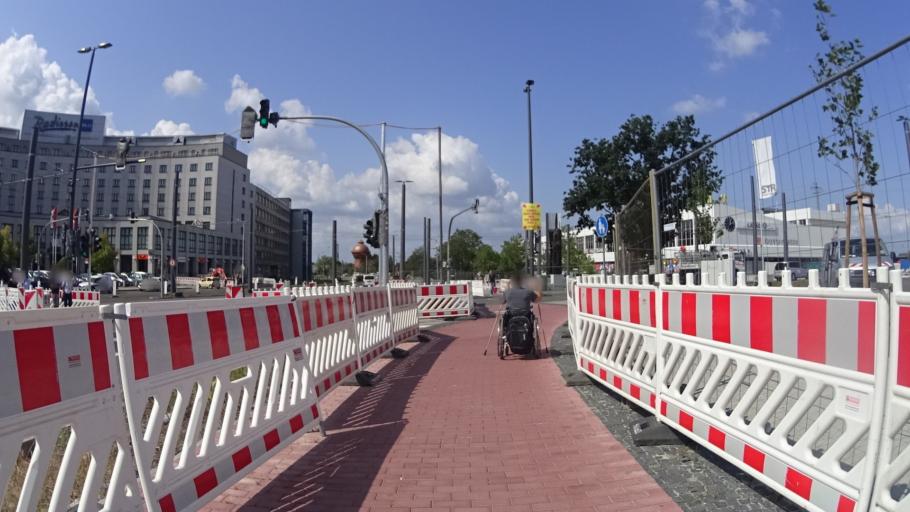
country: DE
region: Brandenburg
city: Cottbus
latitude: 51.7496
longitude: 14.3268
